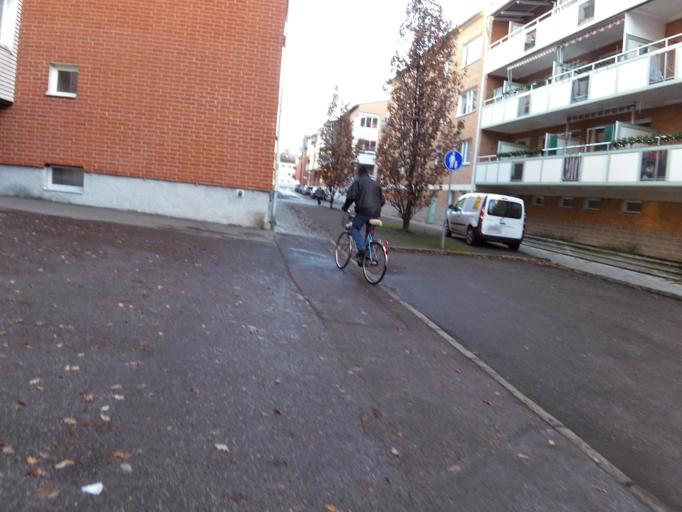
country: SE
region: Gaevleborg
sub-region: Gavle Kommun
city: Gavle
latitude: 60.6693
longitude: 17.1480
